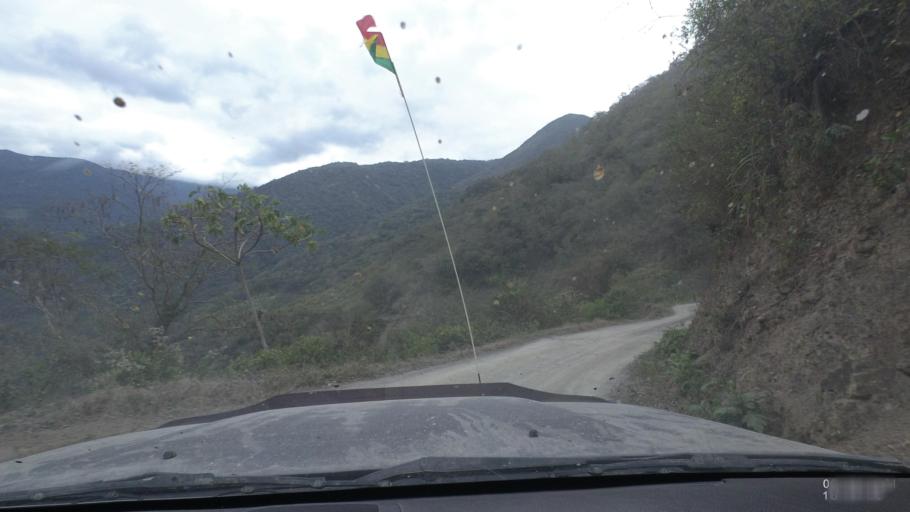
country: BO
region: La Paz
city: Quime
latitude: -16.5338
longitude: -66.7594
